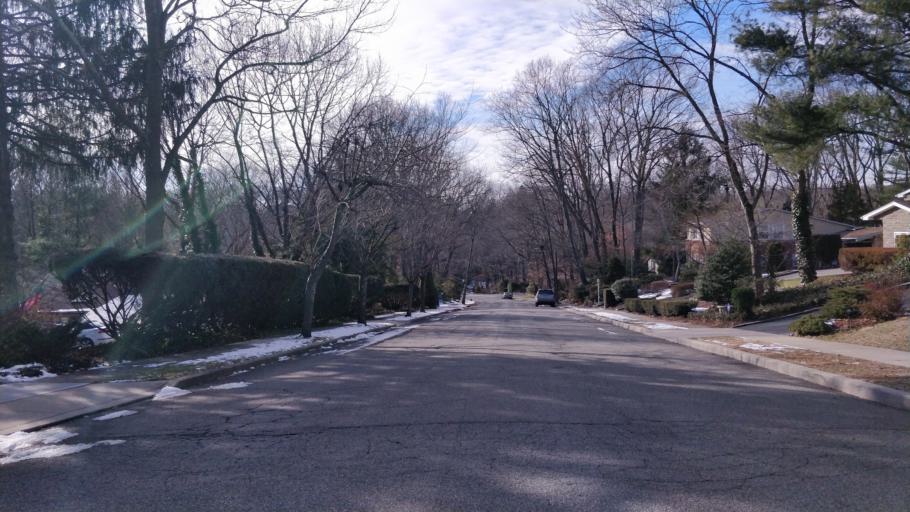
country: US
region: New York
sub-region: Nassau County
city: East Norwich
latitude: 40.8507
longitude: -73.5299
